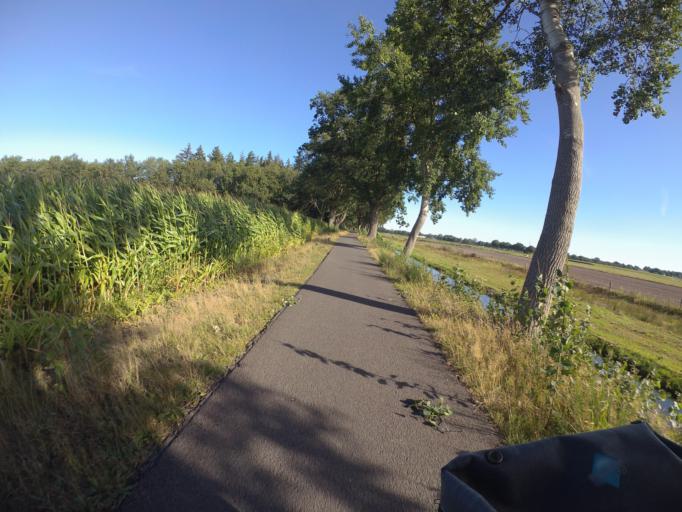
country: NL
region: Drenthe
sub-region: Gemeente Hoogeveen
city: Hoogeveen
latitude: 52.6822
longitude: 6.4660
